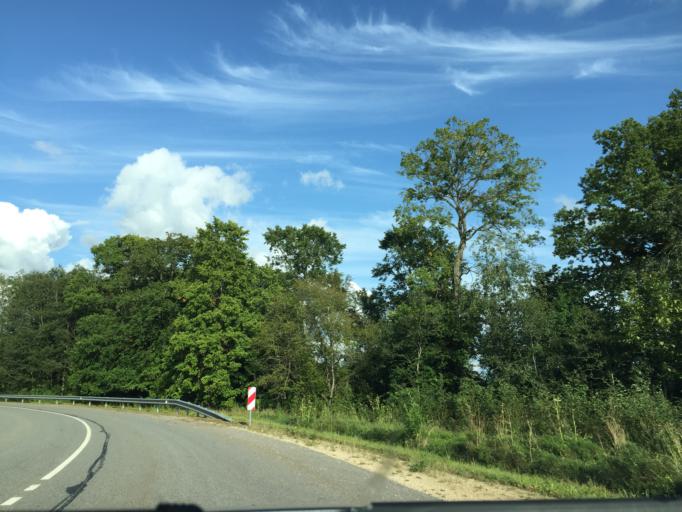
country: LV
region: Kegums
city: Kegums
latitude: 56.8229
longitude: 24.7609
